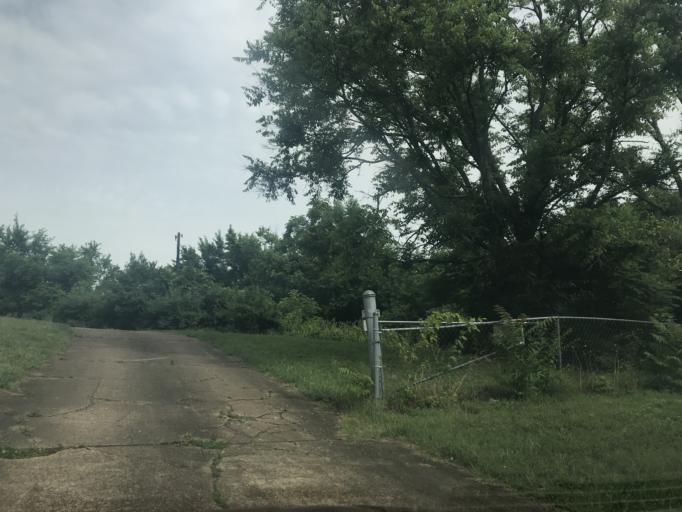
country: US
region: Tennessee
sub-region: Davidson County
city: Nashville
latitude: 36.1975
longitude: -86.8314
